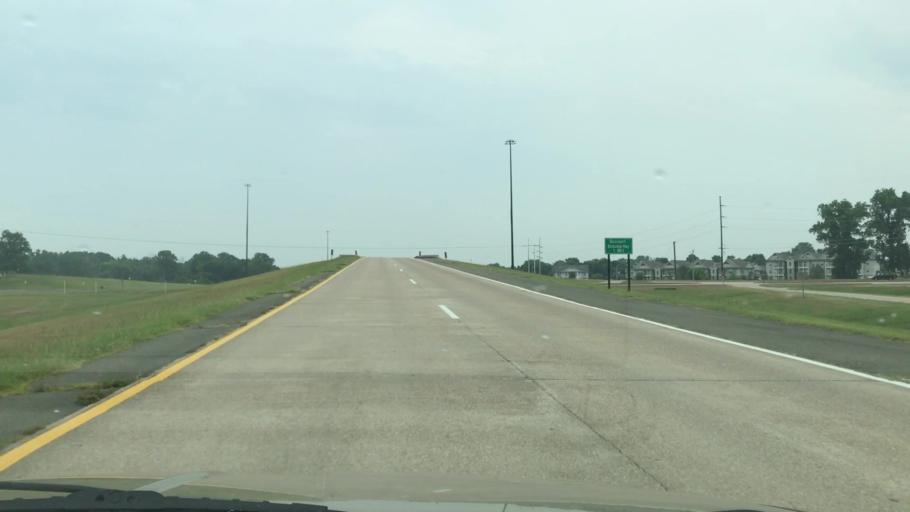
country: US
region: Louisiana
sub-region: Bossier Parish
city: Bossier City
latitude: 32.5016
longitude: -93.7173
